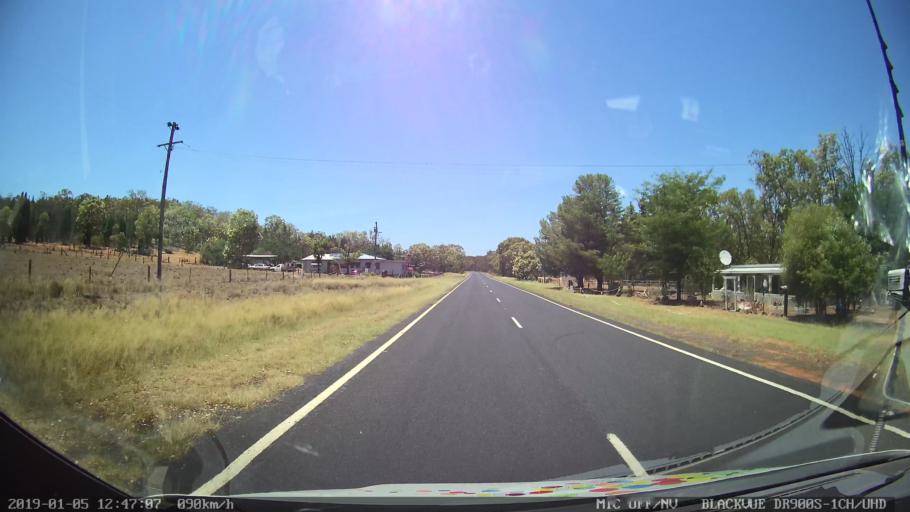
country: AU
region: New South Wales
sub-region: Warrumbungle Shire
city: Coonabarabran
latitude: -31.1162
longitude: 149.5722
